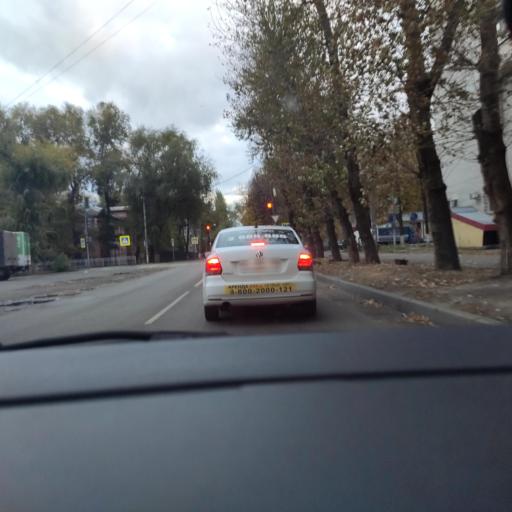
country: RU
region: Voronezj
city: Voronezh
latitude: 51.6877
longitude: 39.1908
